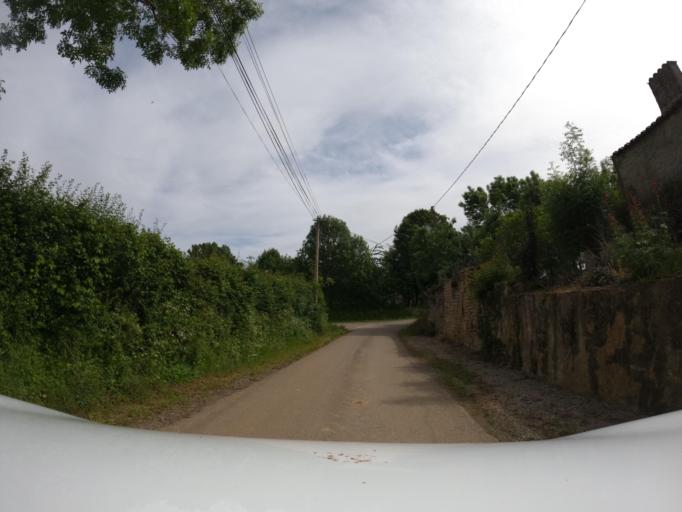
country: FR
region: Pays de la Loire
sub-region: Departement de la Vendee
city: Saint-Hilaire-des-Loges
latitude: 46.4979
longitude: -0.6509
